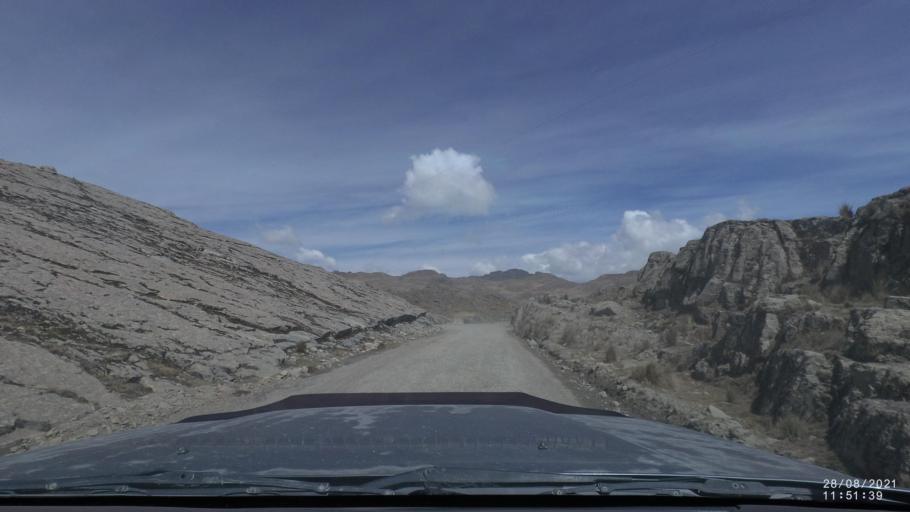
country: BO
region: Cochabamba
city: Sipe Sipe
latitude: -17.2395
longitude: -66.3940
